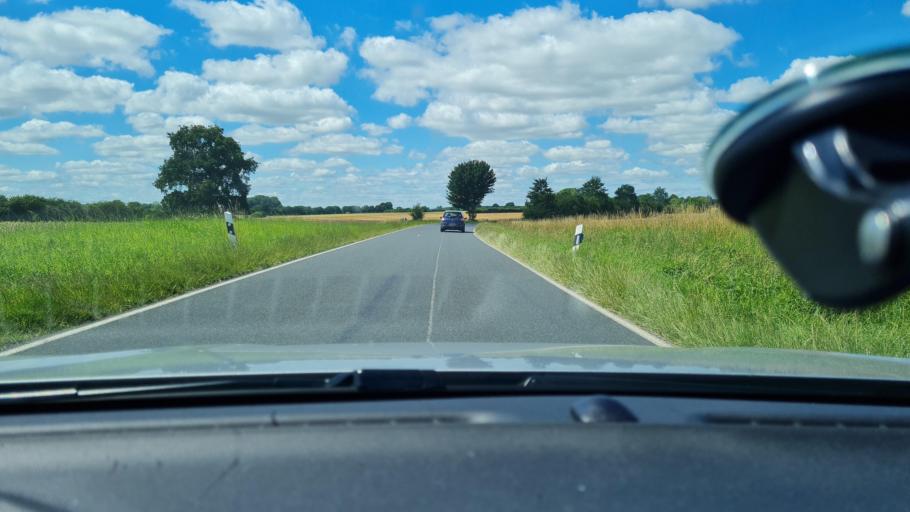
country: DE
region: Schleswig-Holstein
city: Thumby
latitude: 54.5866
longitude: 9.8883
